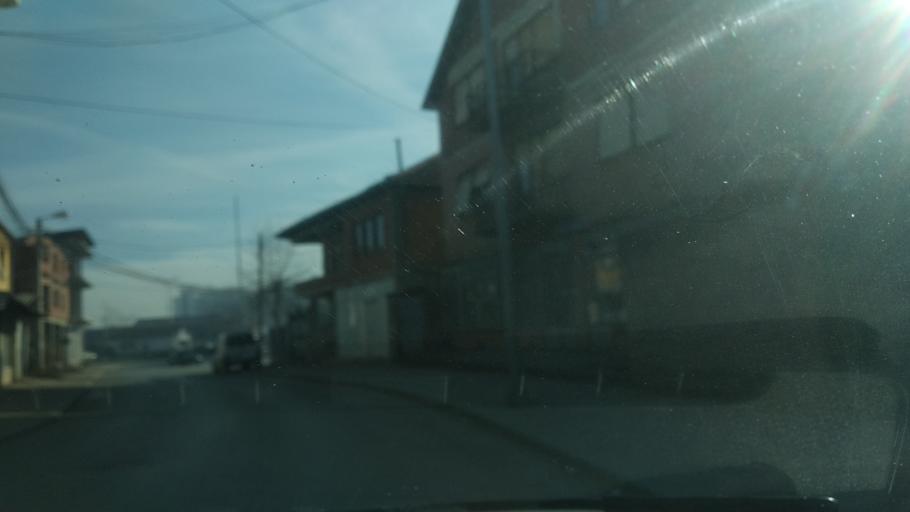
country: XK
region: Mitrovica
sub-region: Vushtrri
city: Vushtrri
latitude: 42.8204
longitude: 20.9752
